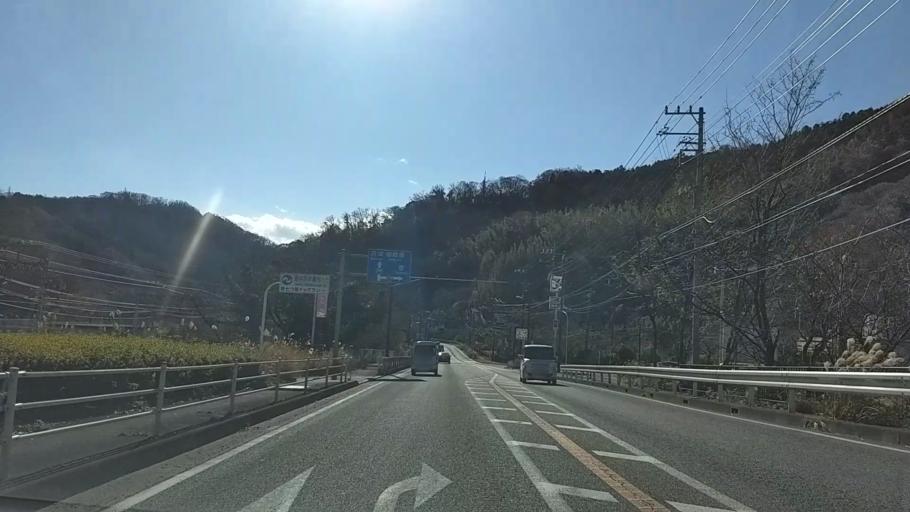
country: JP
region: Kanagawa
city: Hadano
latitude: 35.3638
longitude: 139.1588
